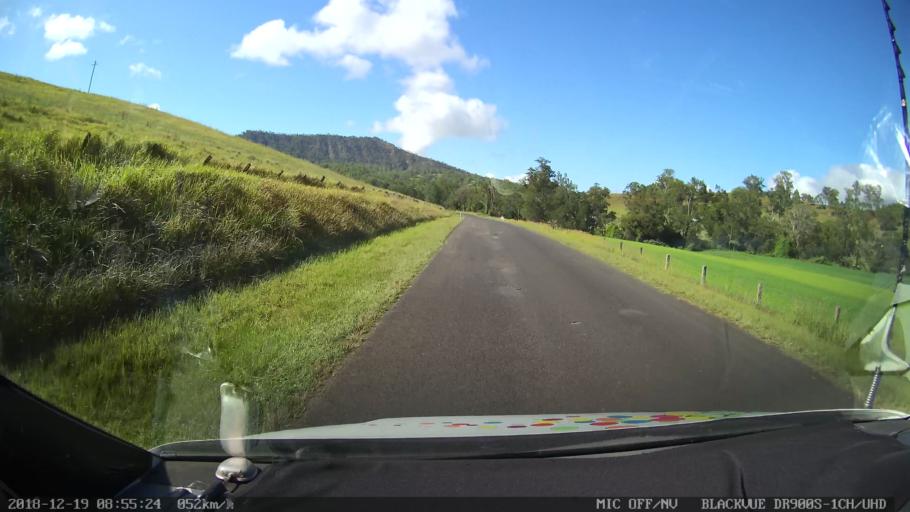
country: AU
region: New South Wales
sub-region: Kyogle
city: Kyogle
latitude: -28.4142
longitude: 152.9781
